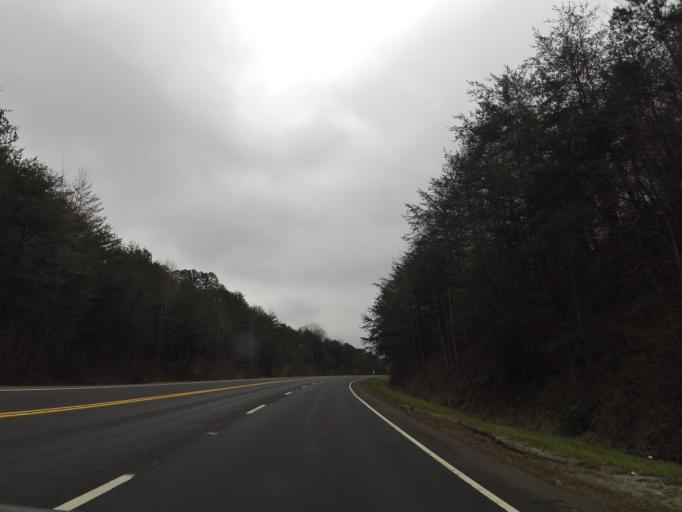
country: US
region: Tennessee
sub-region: Scott County
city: Huntsville
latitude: 36.4005
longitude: -84.4423
